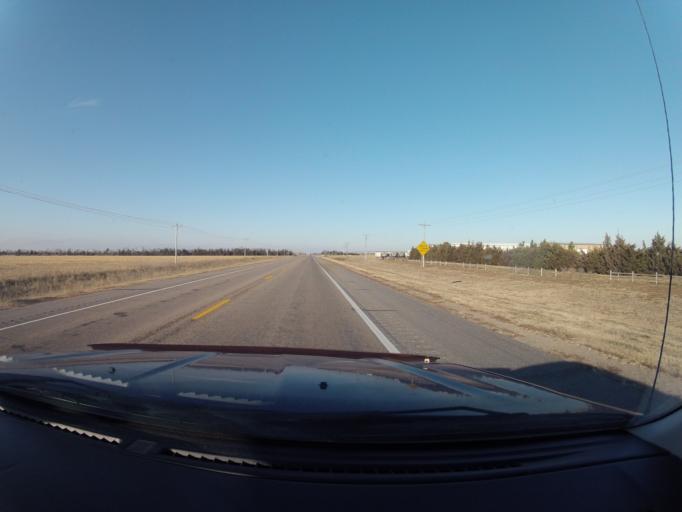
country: US
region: Nebraska
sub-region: Kearney County
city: Minden
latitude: 40.6271
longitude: -98.9515
